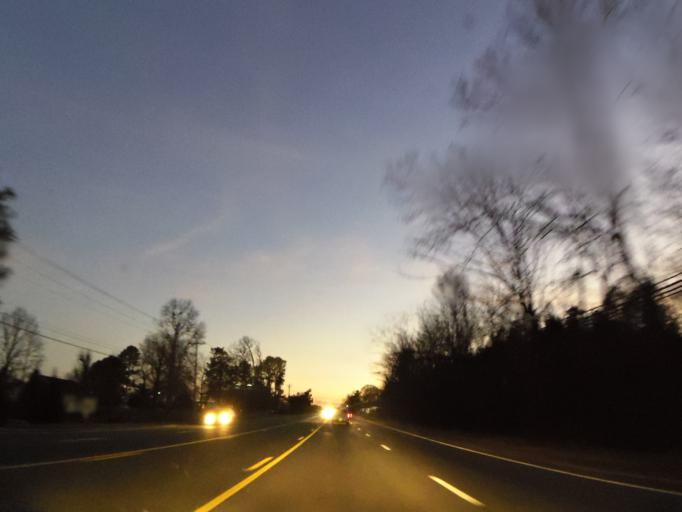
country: US
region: Georgia
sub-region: Whitfield County
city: Dalton
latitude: 34.8280
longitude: -84.9441
